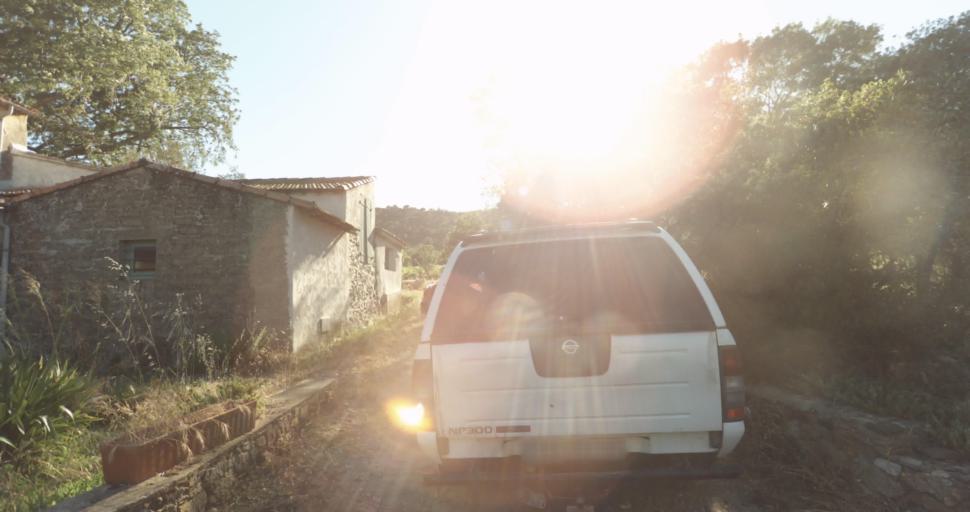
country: FR
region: Provence-Alpes-Cote d'Azur
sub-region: Departement du Var
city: Gassin
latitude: 43.2392
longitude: 6.5933
